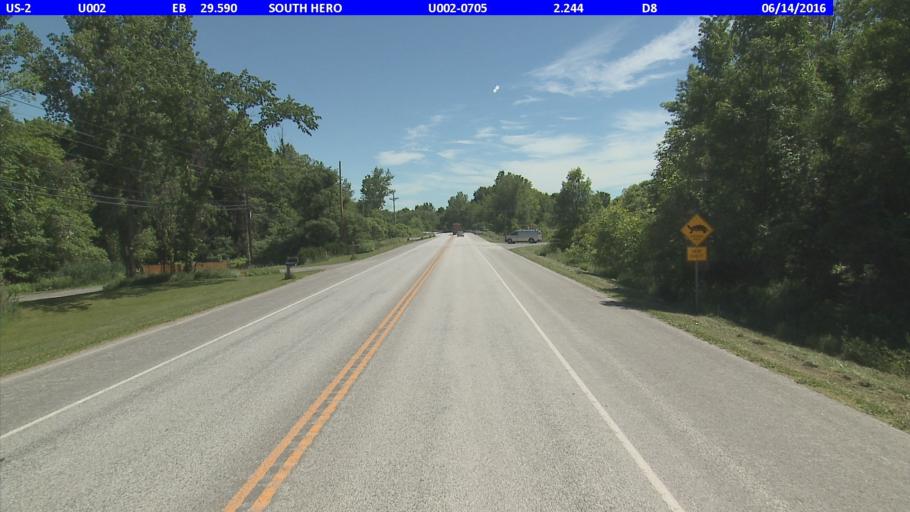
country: US
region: New York
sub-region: Clinton County
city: Cumberland Head
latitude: 44.6497
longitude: -73.3160
